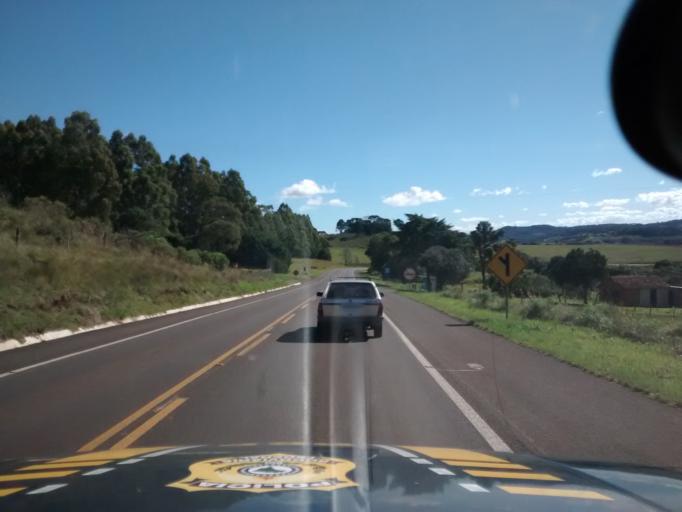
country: BR
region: Rio Grande do Sul
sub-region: Vacaria
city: Vacaria
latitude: -28.3539
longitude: -51.1380
